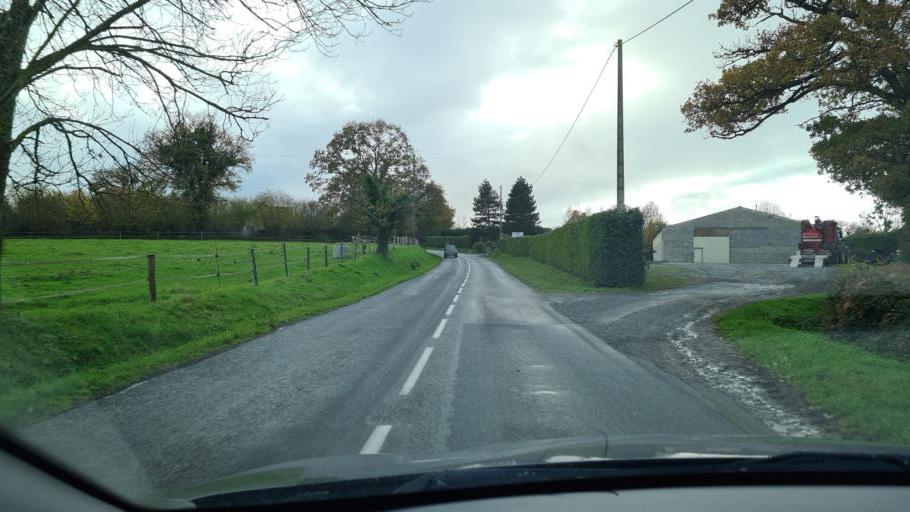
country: FR
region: Lower Normandy
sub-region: Departement de la Manche
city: La Haye-Pesnel
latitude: 48.7901
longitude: -1.4079
